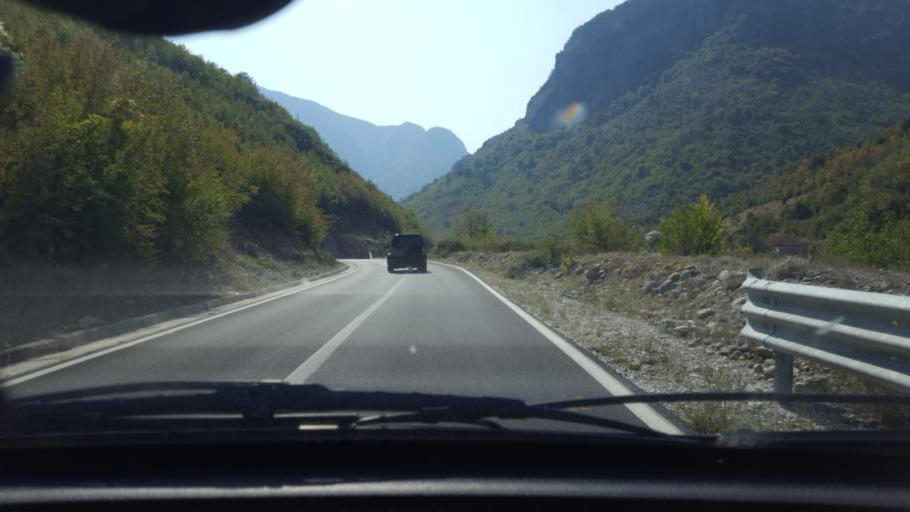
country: AL
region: Shkoder
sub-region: Rrethi i Malesia e Madhe
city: Kastrat
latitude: 42.4448
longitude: 19.5419
